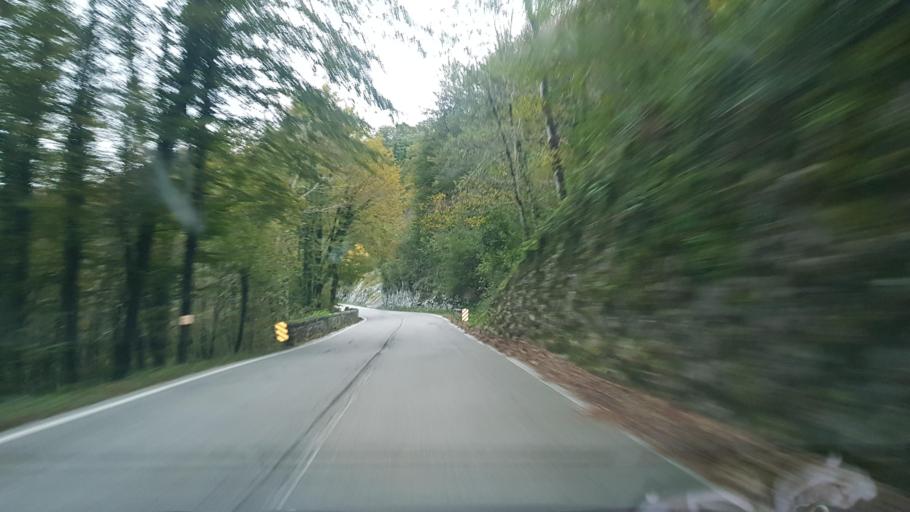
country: IT
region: Friuli Venezia Giulia
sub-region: Provincia di Pordenone
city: Anduins
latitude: 46.2755
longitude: 12.9396
